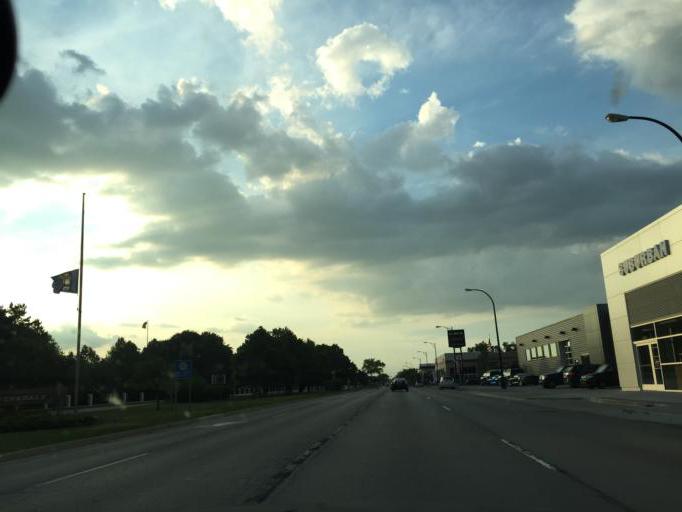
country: US
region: Michigan
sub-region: Oakland County
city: Ferndale
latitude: 42.4509
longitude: -83.1277
